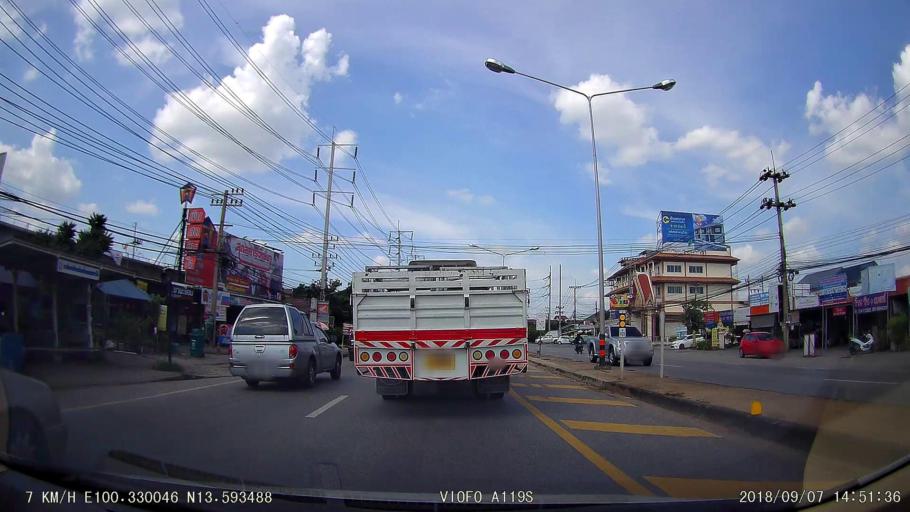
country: TH
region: Samut Sakhon
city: Samut Sakhon
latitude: 13.5935
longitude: 100.3301
